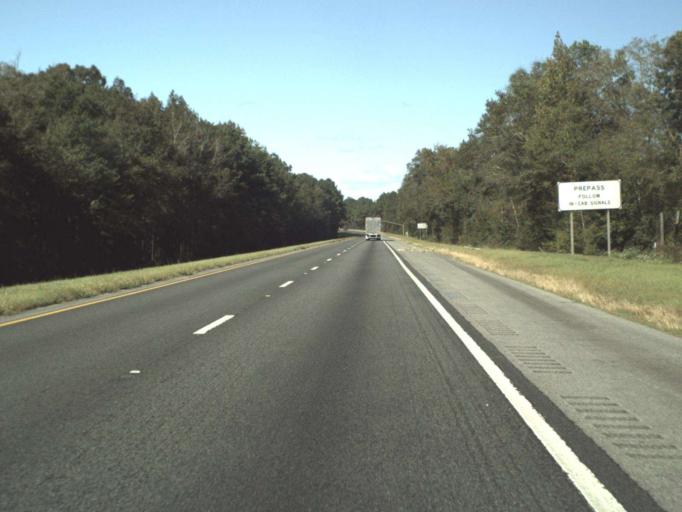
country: US
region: Florida
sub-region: Jackson County
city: Sneads
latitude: 30.6389
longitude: -84.9567
